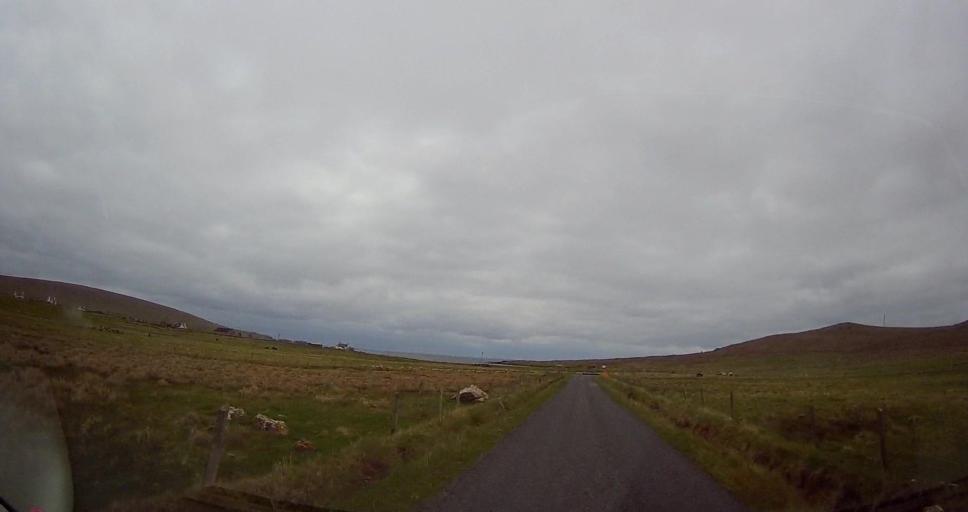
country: GB
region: Scotland
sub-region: Shetland Islands
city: Shetland
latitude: 60.7897
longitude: -0.8432
